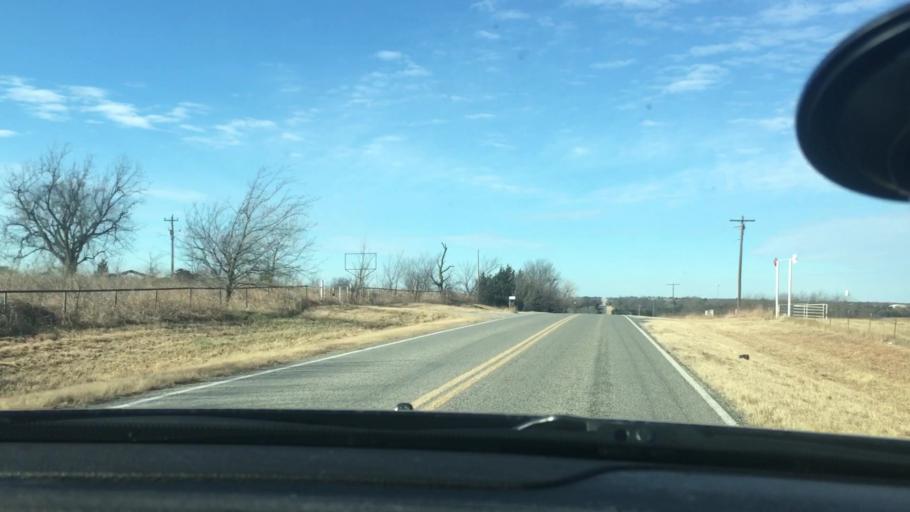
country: US
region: Oklahoma
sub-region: Seminole County
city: Konawa
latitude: 34.9859
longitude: -96.9042
